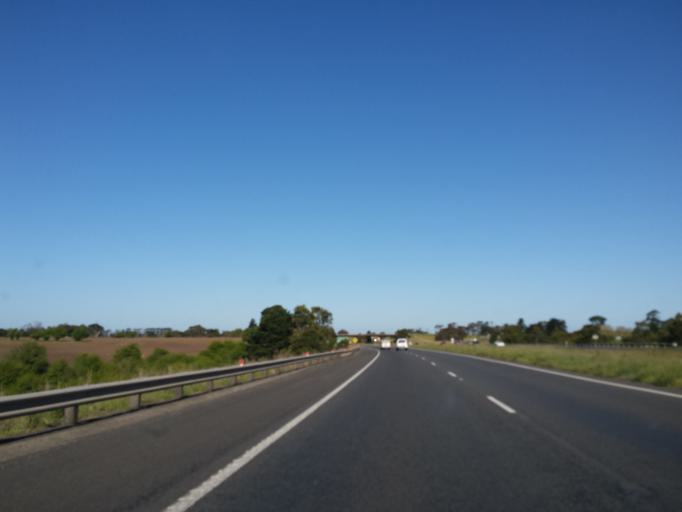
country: AU
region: Victoria
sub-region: Moorabool
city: Bacchus Marsh
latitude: -37.5957
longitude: 144.2537
